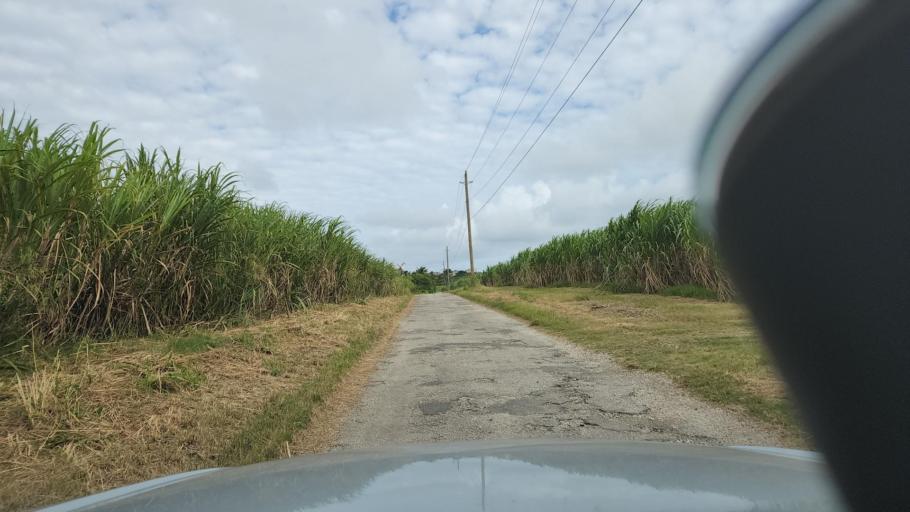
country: BB
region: Saint Lucy
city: Checker Hall
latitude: 13.2962
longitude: -59.6129
